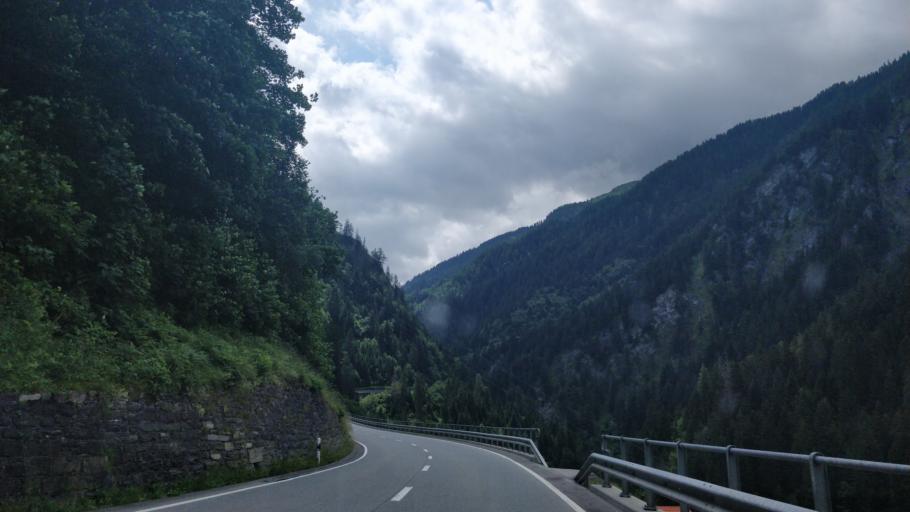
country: CH
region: Grisons
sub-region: Surselva District
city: Ilanz
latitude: 46.6752
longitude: 9.1809
